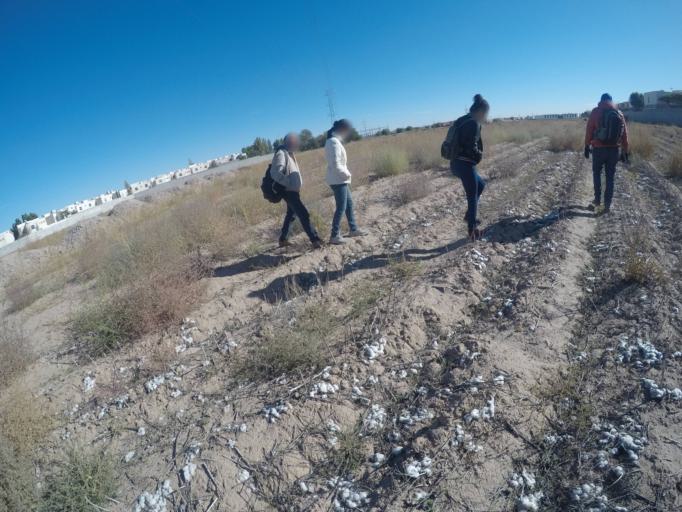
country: US
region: Texas
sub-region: El Paso County
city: Socorro
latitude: 31.6985
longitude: -106.3782
